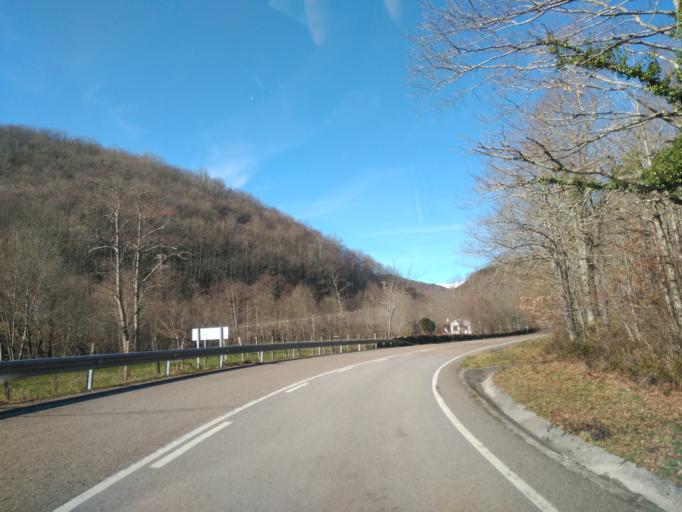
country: ES
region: Cantabria
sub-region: Provincia de Cantabria
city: Ruente
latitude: 43.1515
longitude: -4.2202
